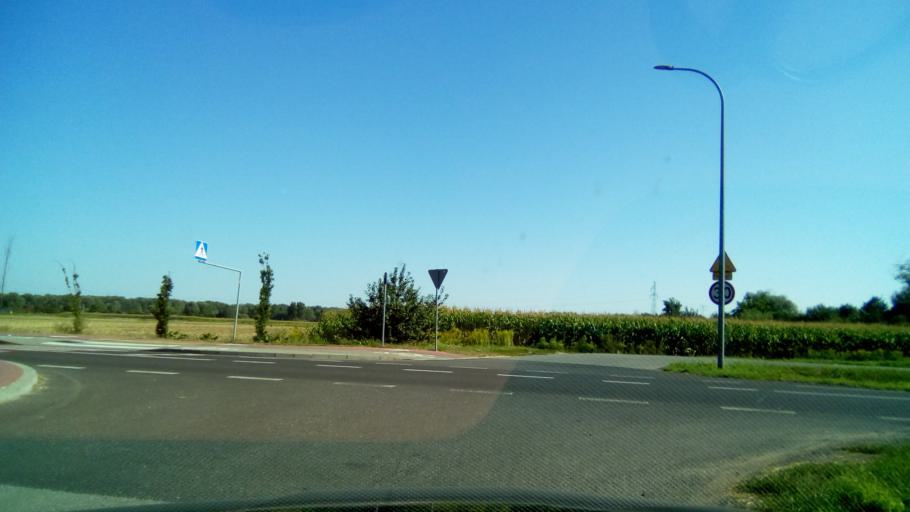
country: PL
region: Masovian Voivodeship
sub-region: Plock
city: Plock
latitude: 52.5110
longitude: 19.7063
